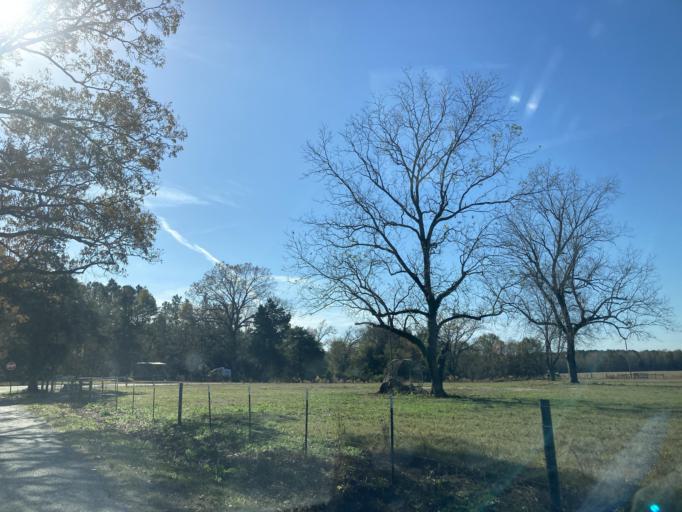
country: US
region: Mississippi
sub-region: Lamar County
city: Sumrall
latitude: 31.2677
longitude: -89.5308
